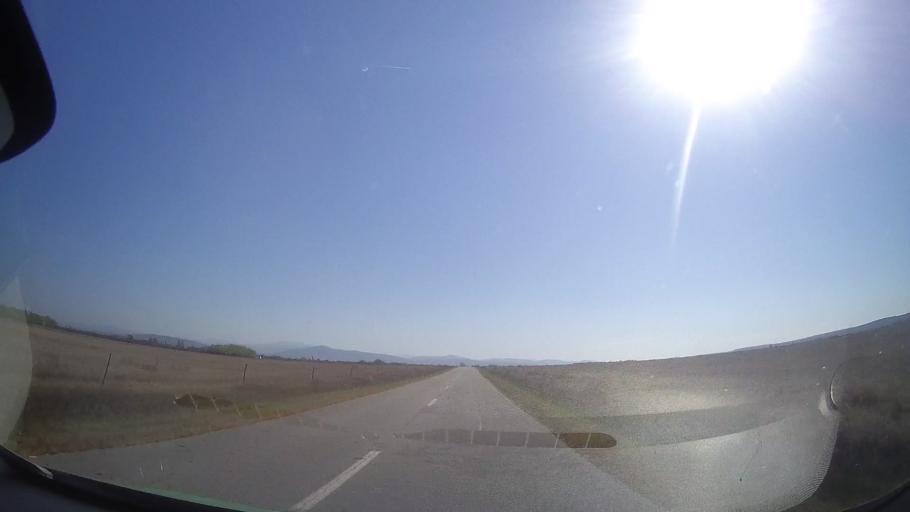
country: RO
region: Timis
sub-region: Comuna Traian Vuia
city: Traian Vuia
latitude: 45.7970
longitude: 22.0125
